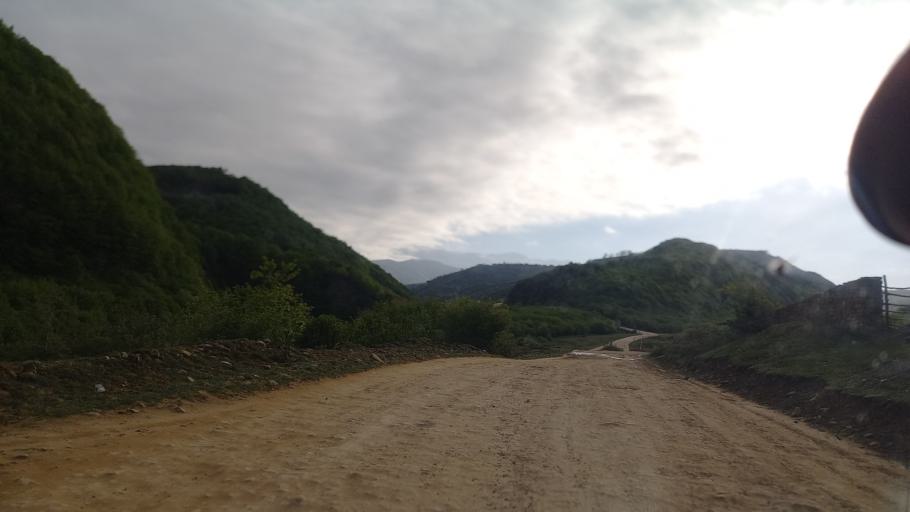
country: RU
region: Dagestan
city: Khuchni
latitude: 41.9618
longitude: 47.8679
